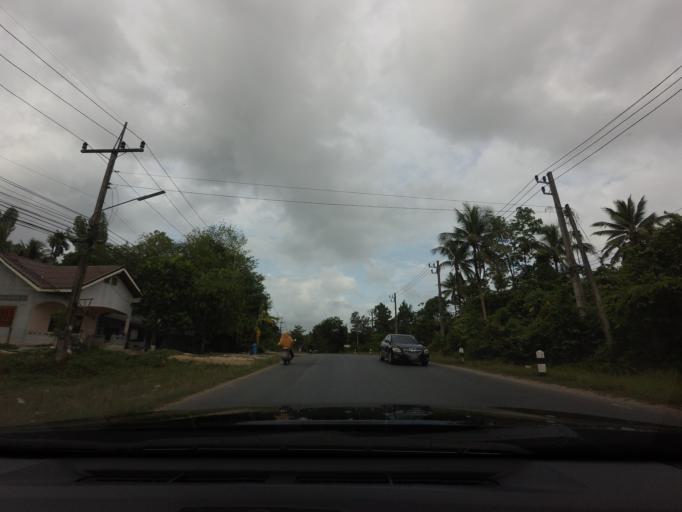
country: TH
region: Yala
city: Raman
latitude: 6.4750
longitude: 101.4036
